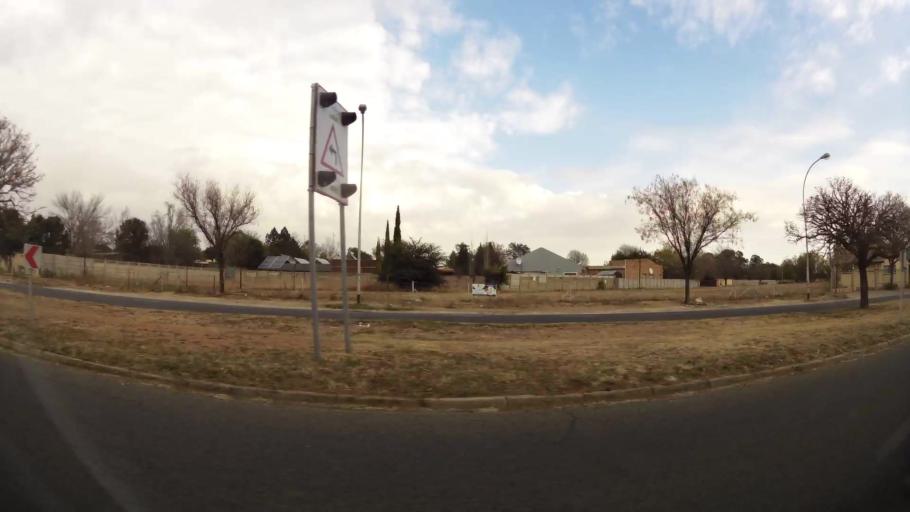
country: ZA
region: Orange Free State
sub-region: Mangaung Metropolitan Municipality
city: Bloemfontein
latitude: -29.1205
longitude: 26.1647
